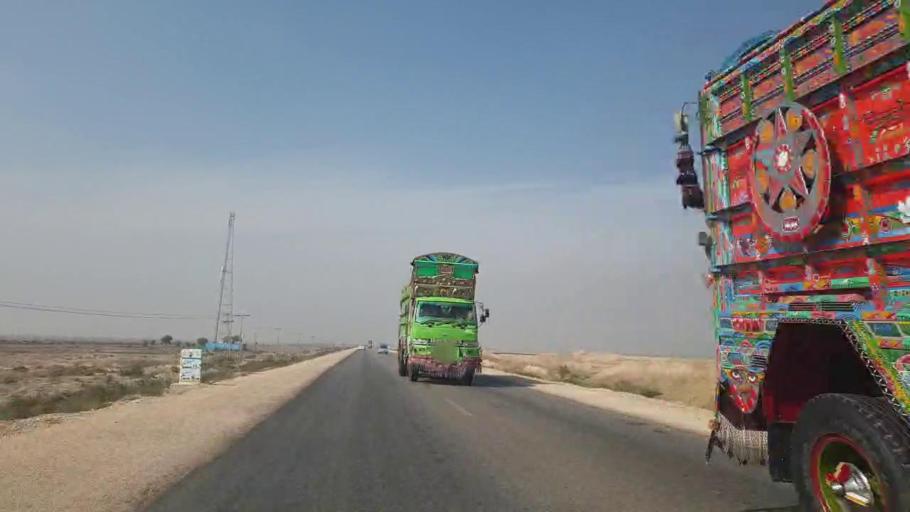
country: PK
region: Sindh
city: Sann
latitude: 25.9212
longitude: 68.2172
